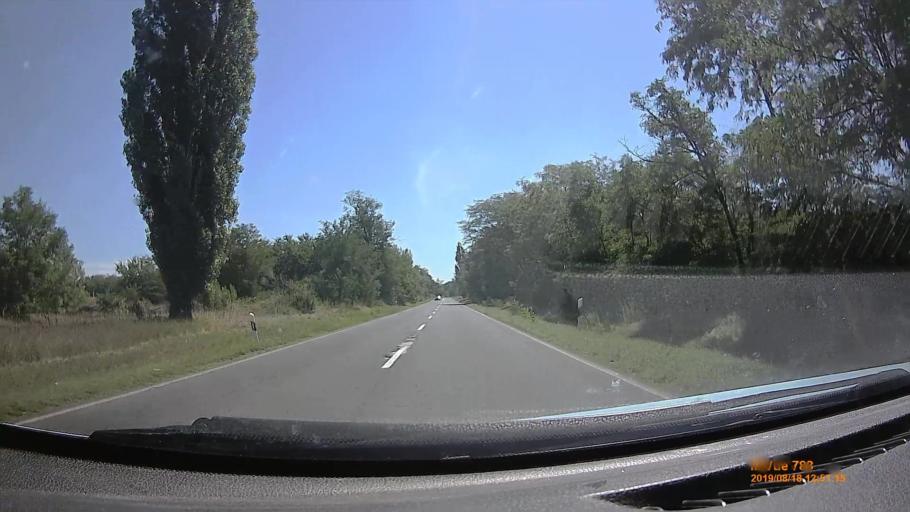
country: HU
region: Fejer
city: Aba
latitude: 47.0756
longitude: 18.5069
